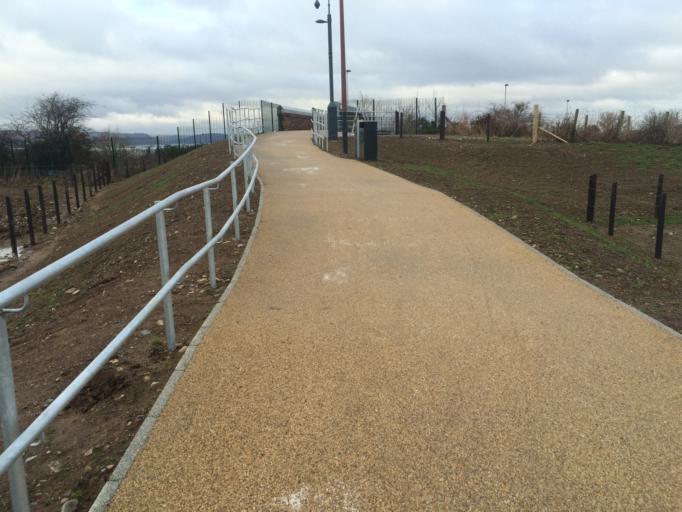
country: GB
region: Scotland
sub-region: Highland
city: Inverness
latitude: 57.4765
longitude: -4.1754
